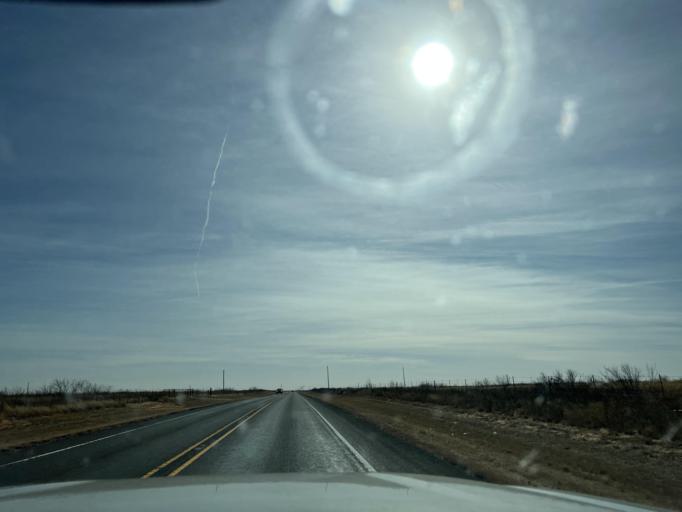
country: US
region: Texas
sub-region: Andrews County
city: Andrews
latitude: 32.4309
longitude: -102.4377
